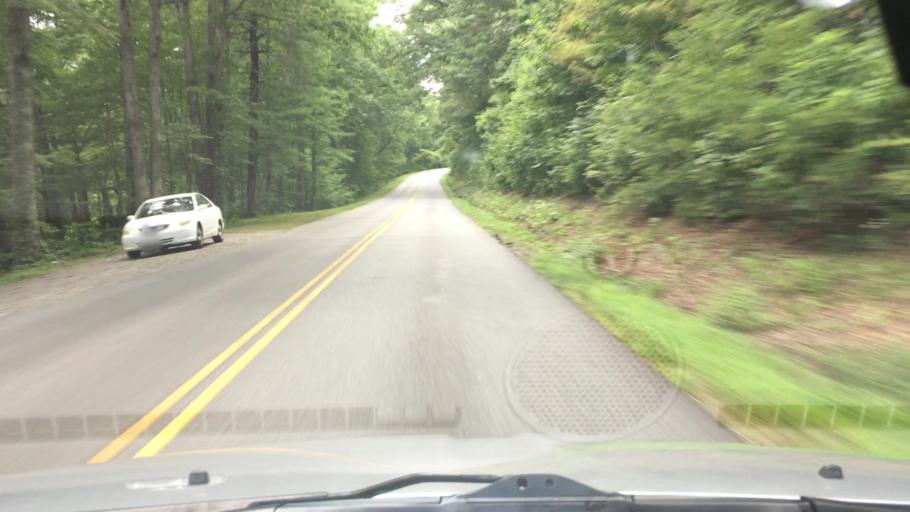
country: US
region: North Carolina
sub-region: Buncombe County
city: Asheville
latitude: 35.6059
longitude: -82.4907
